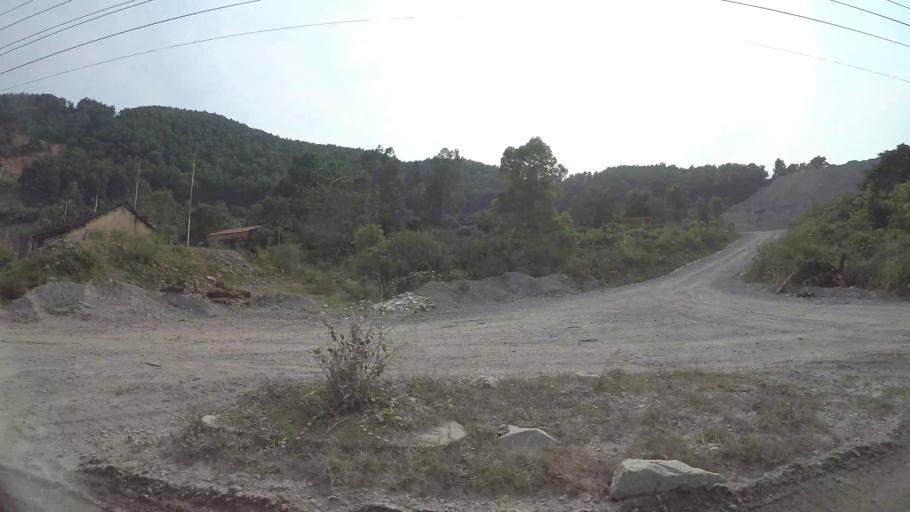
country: VN
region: Da Nang
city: Lien Chieu
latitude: 16.0393
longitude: 108.1522
